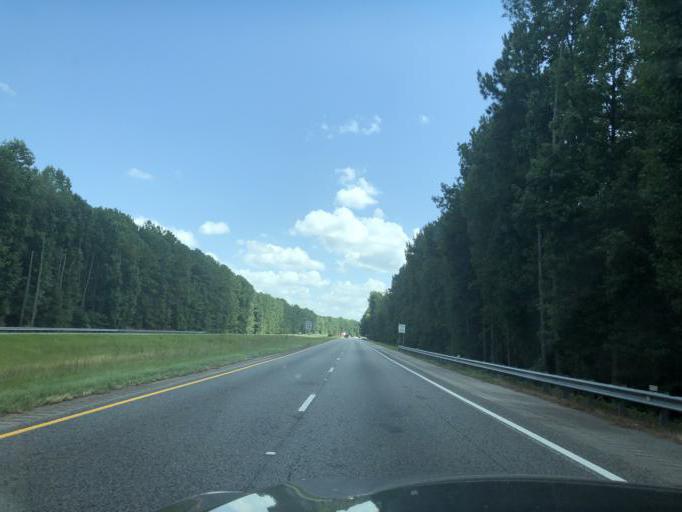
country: US
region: Georgia
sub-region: Troup County
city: La Grange
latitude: 32.9974
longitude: -84.9531
